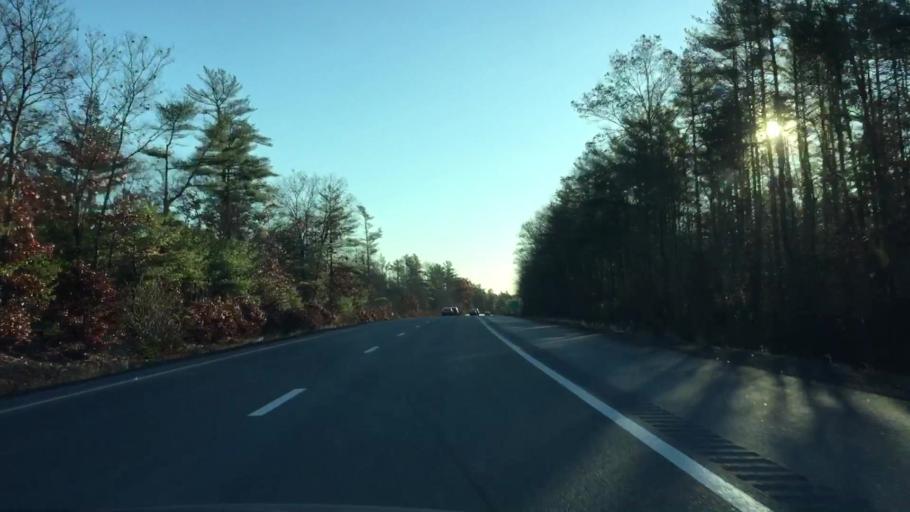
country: US
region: Massachusetts
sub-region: Plymouth County
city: Carver
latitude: 41.8438
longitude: -70.8386
